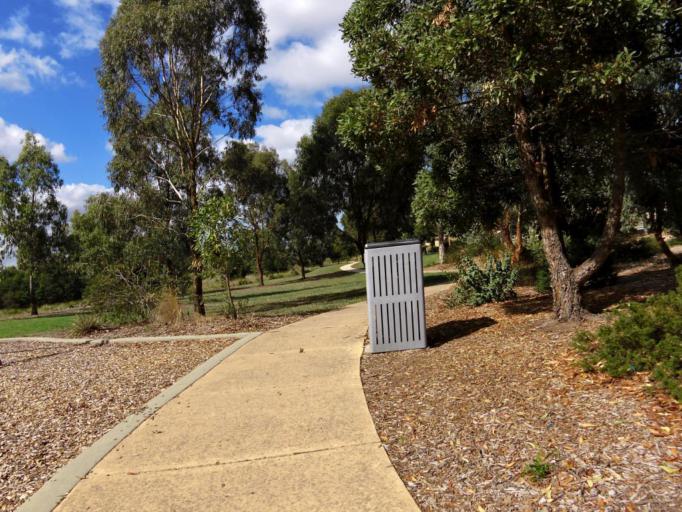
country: AU
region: Victoria
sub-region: Whittlesea
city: Mernda
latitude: -37.6214
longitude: 145.0687
